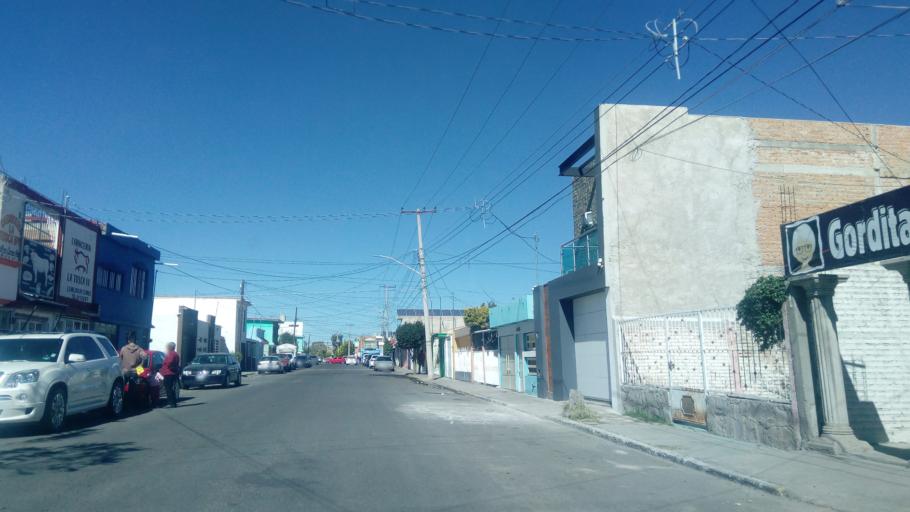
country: MX
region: Durango
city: Victoria de Durango
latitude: 24.0187
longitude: -104.6408
